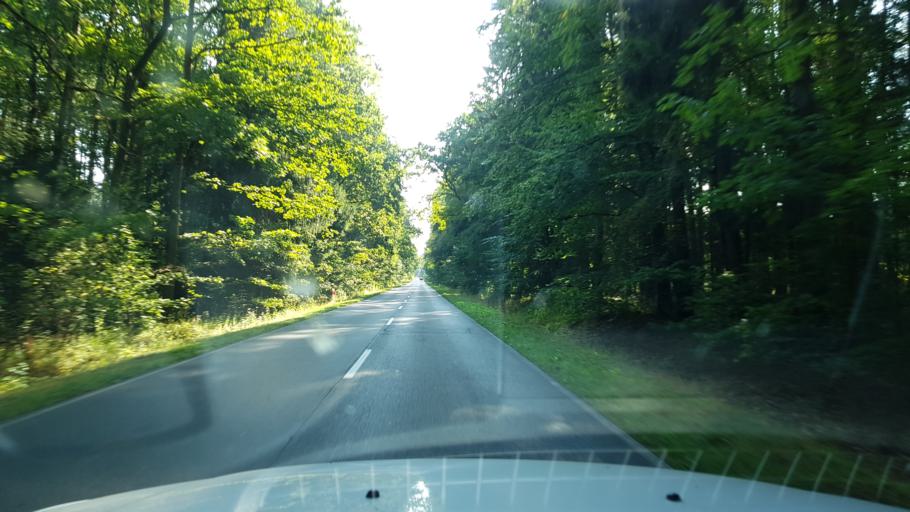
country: PL
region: West Pomeranian Voivodeship
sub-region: Powiat lobeski
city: Resko
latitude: 53.7712
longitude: 15.4529
